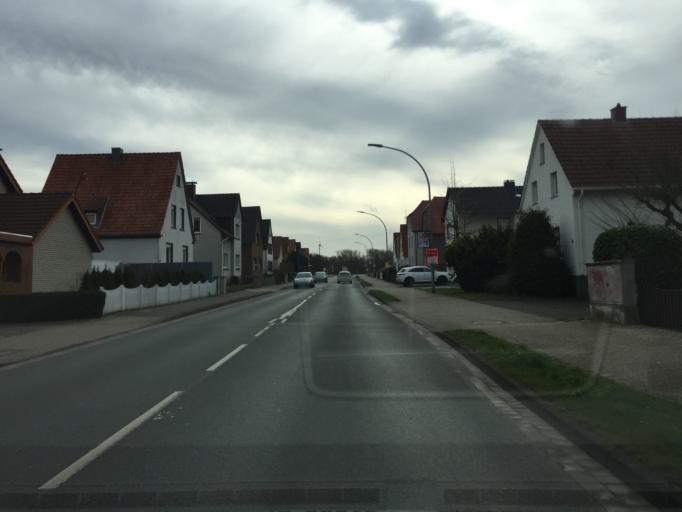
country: DE
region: North Rhine-Westphalia
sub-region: Regierungsbezirk Detmold
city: Lage
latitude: 51.9830
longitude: 8.7958
